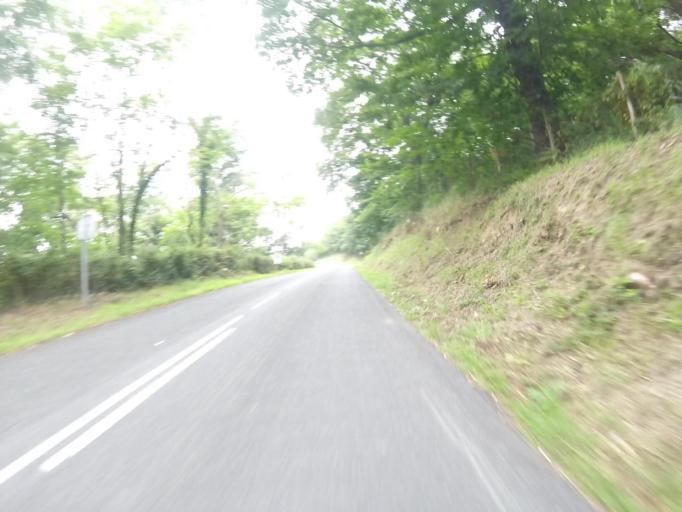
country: ES
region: Basque Country
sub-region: Provincia de Guipuzcoa
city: Lezo
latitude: 43.3130
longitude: -1.8464
